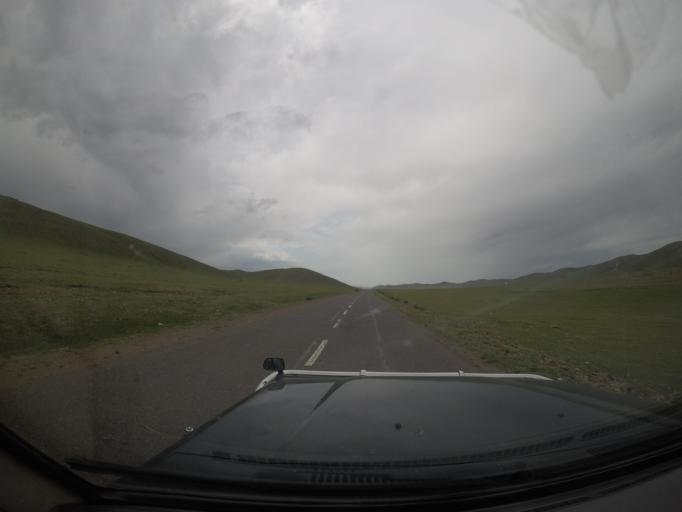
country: MN
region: Hentiy
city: Modot
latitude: 47.6949
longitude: 109.0842
